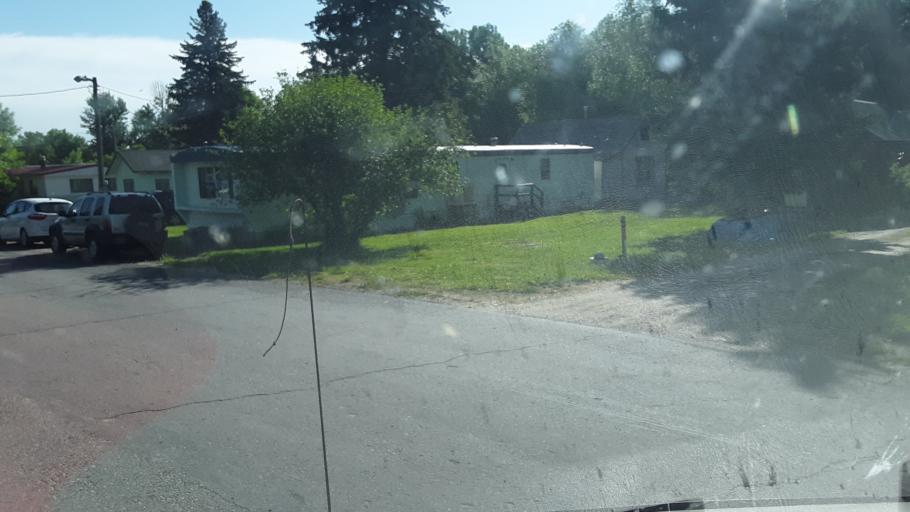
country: US
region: Montana
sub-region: Carbon County
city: Red Lodge
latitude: 45.3578
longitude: -109.1651
